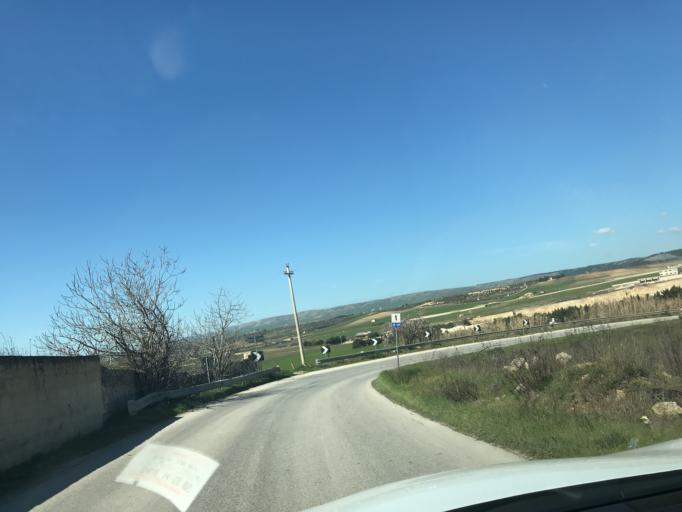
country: IT
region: Apulia
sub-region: Provincia di Bari
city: Gravina in Puglia
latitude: 40.8359
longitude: 16.4257
